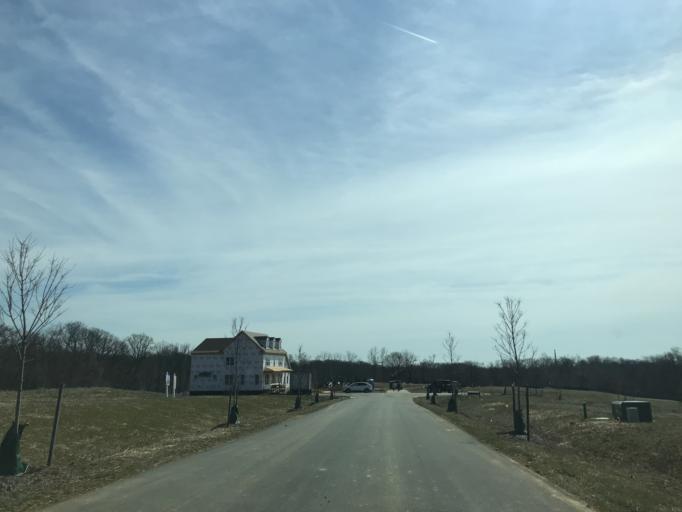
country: US
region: Maryland
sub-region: Howard County
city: Highland
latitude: 39.1630
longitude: -76.9433
